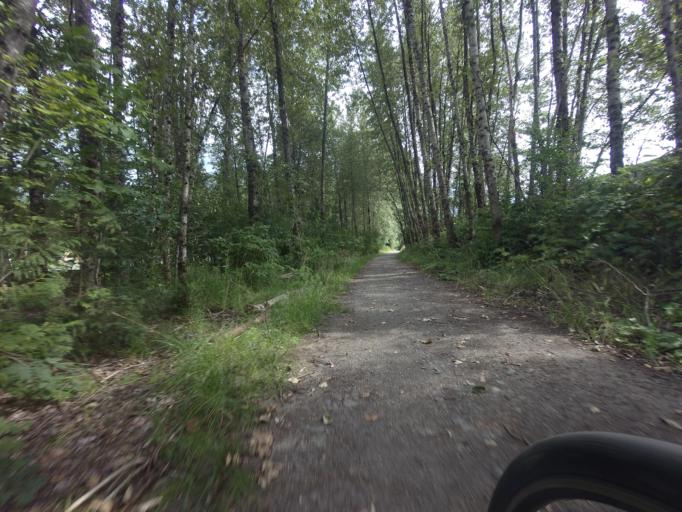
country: CA
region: British Columbia
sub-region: Greater Vancouver Regional District
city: Lions Bay
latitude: 49.7073
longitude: -123.1492
